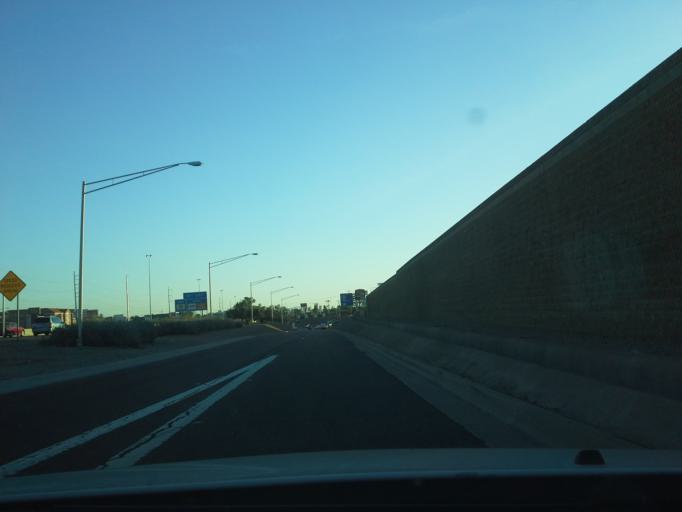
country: US
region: Arizona
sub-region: Maricopa County
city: Glendale
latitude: 33.5853
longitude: -112.1174
